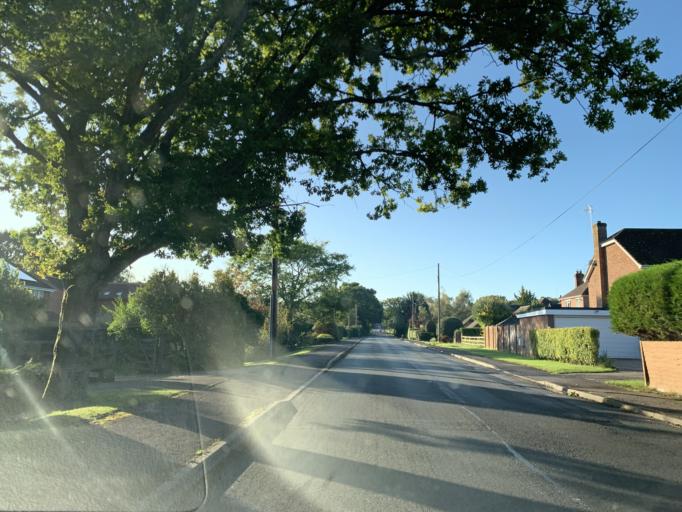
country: GB
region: England
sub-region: Wiltshire
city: Whiteparish
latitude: 50.9707
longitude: -1.6365
